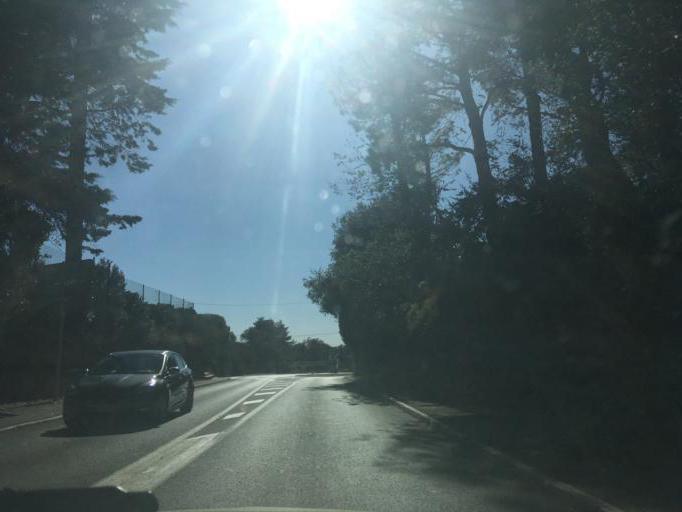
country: FR
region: Provence-Alpes-Cote d'Azur
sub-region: Departement du Var
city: La Garde-Freinet
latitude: 43.3139
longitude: 6.4713
